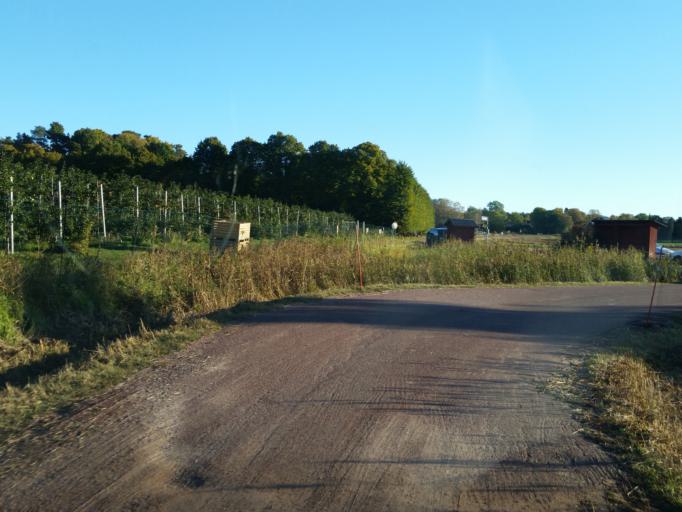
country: AX
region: Alands skaergard
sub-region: Vardoe
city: Vardoe
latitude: 60.2434
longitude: 20.3406
